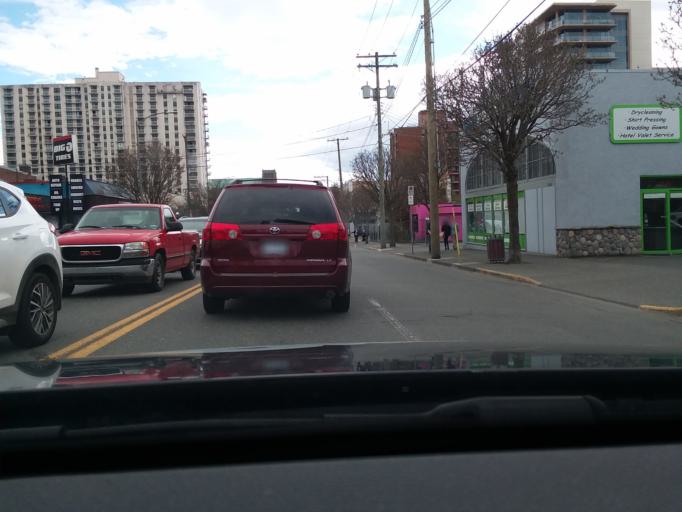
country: CA
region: British Columbia
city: Victoria
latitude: 48.4265
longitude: -123.3591
